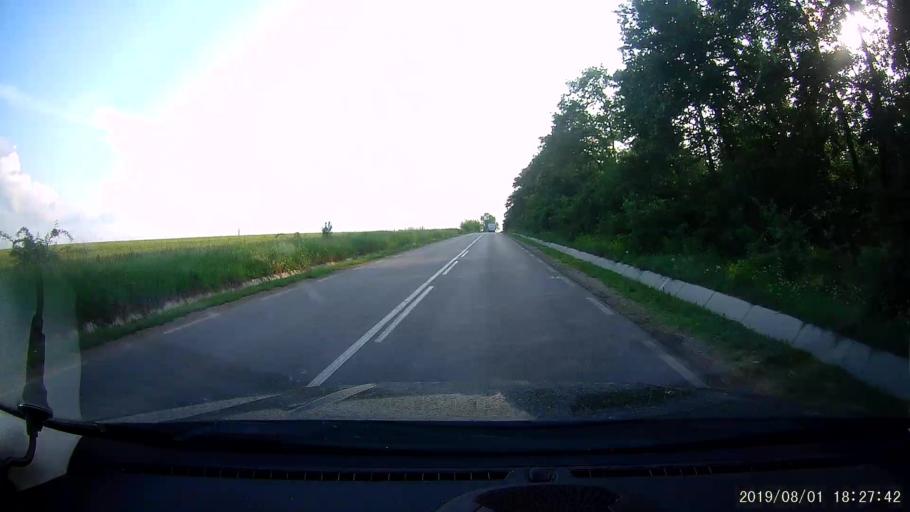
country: BG
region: Shumen
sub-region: Obshtina Venets
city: Venets
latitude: 43.5827
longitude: 26.9788
